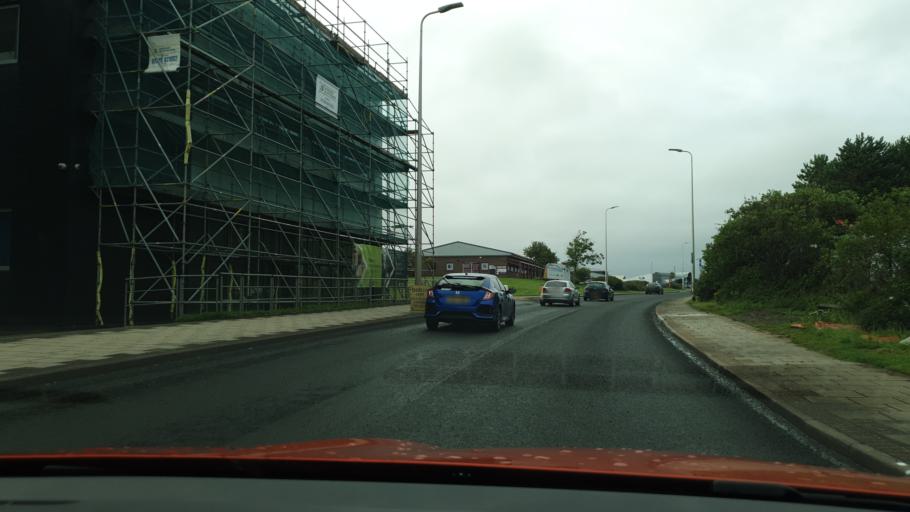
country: GB
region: England
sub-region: Cumbria
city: Barrow in Furness
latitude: 54.1166
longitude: -3.2415
